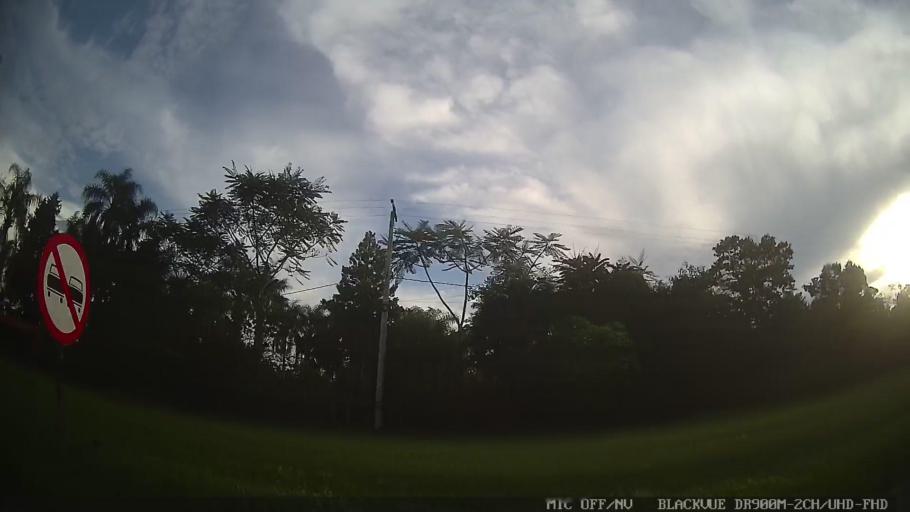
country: BR
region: Sao Paulo
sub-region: Porto Feliz
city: Porto Feliz
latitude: -23.1958
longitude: -47.6218
